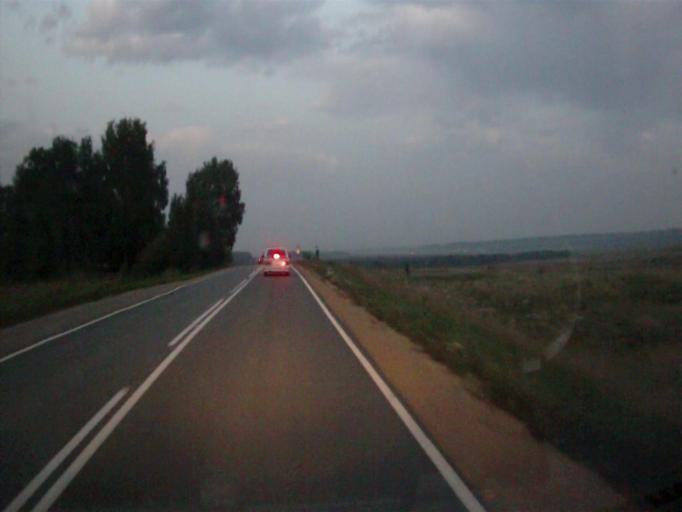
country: RU
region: Chelyabinsk
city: Argayash
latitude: 55.2088
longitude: 60.8457
